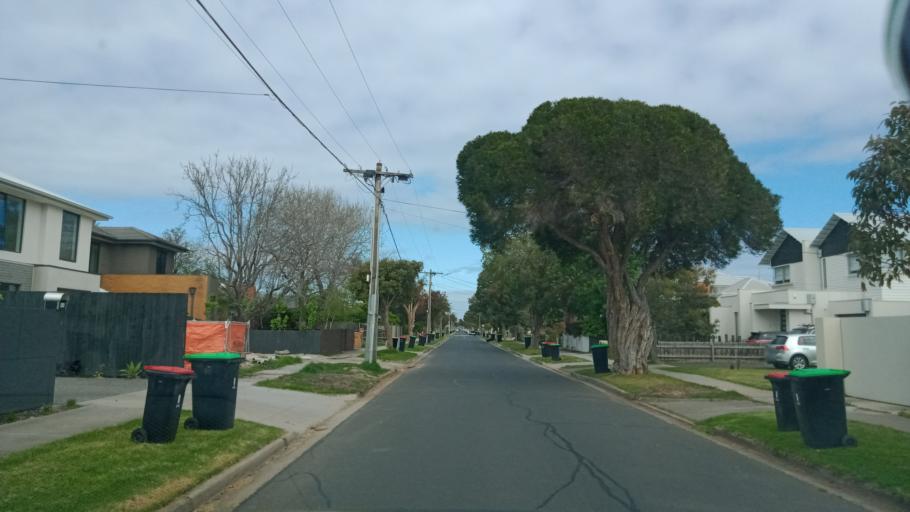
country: AU
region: Victoria
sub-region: Kingston
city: Edithvale
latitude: -38.0331
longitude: 145.1157
